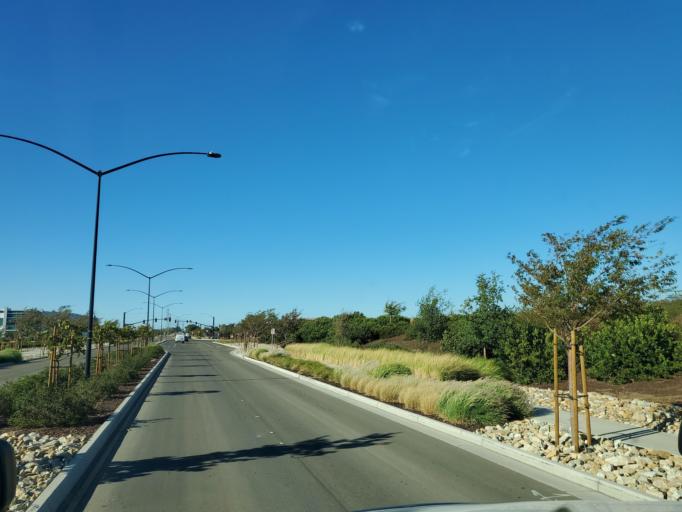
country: US
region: California
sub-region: San Joaquin County
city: Mountain House
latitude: 37.7312
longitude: -121.5131
